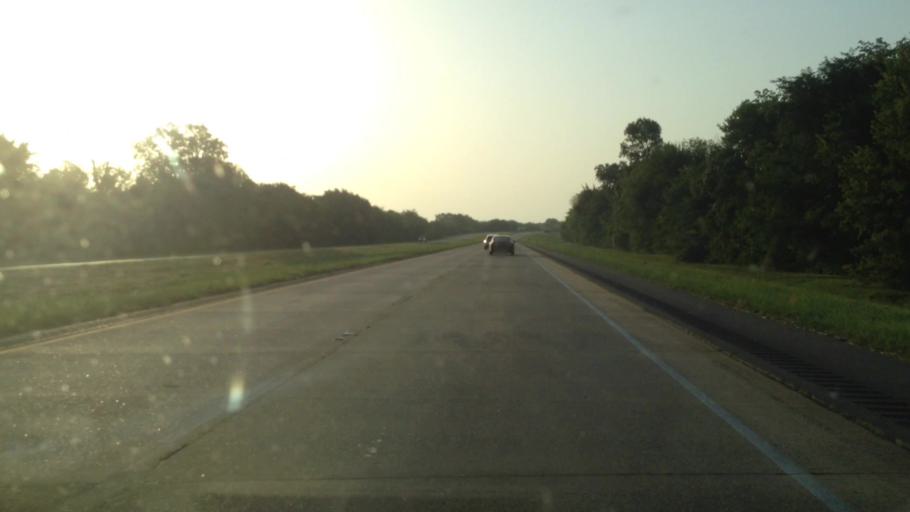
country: US
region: Louisiana
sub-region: Natchitoches Parish
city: Vienna Bend
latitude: 31.5691
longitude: -93.0032
